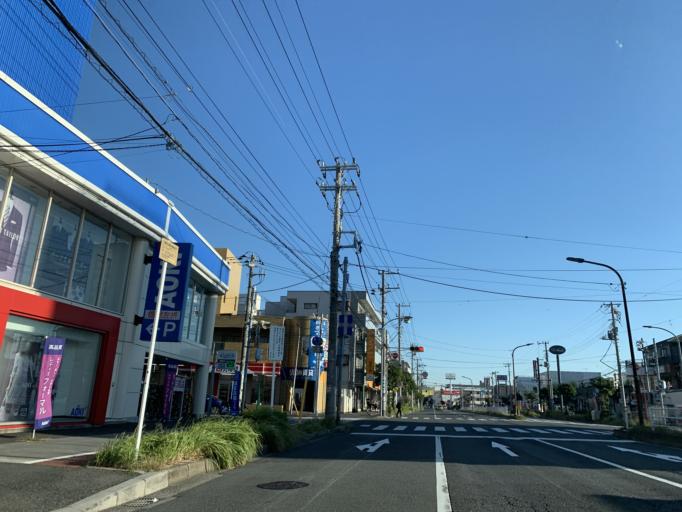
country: JP
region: Tokyo
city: Urayasu
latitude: 35.6715
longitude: 139.9012
